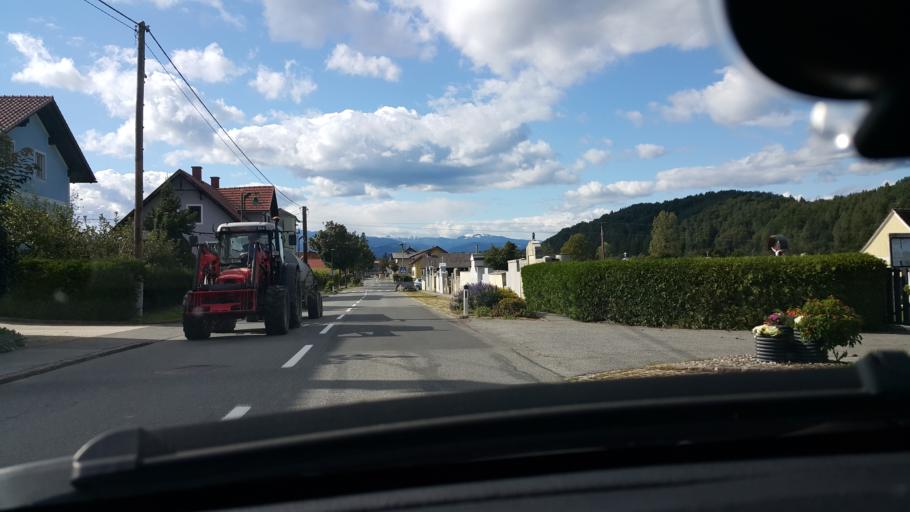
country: AT
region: Styria
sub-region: Politischer Bezirk Leibnitz
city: Oberhaag
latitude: 46.6848
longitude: 15.3380
